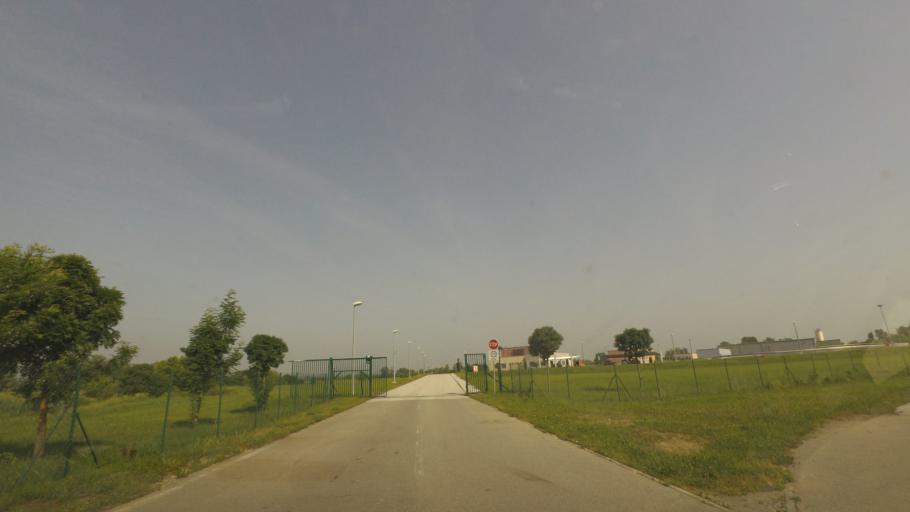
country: HR
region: Karlovacka
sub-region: Grad Karlovac
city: Karlovac
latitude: 45.4892
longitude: 15.5870
